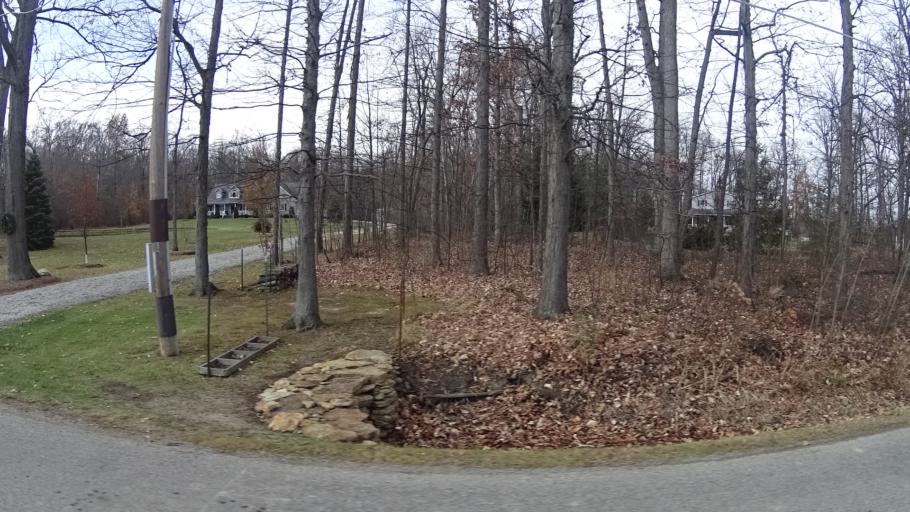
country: US
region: Ohio
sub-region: Lorain County
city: Eaton Estates
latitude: 41.2493
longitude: -81.9731
